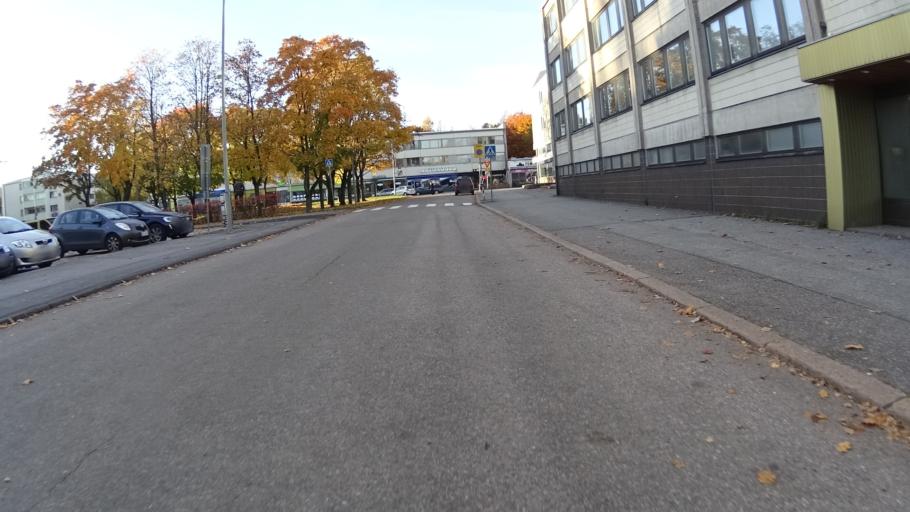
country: FI
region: Uusimaa
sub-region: Helsinki
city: Helsinki
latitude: 60.2295
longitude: 24.9663
